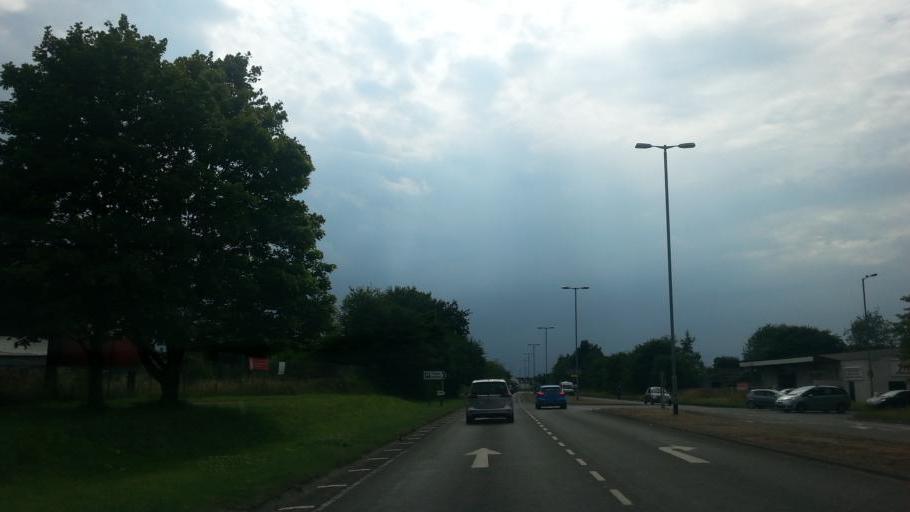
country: GB
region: England
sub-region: Norfolk
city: Briston
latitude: 52.9040
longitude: 1.0944
